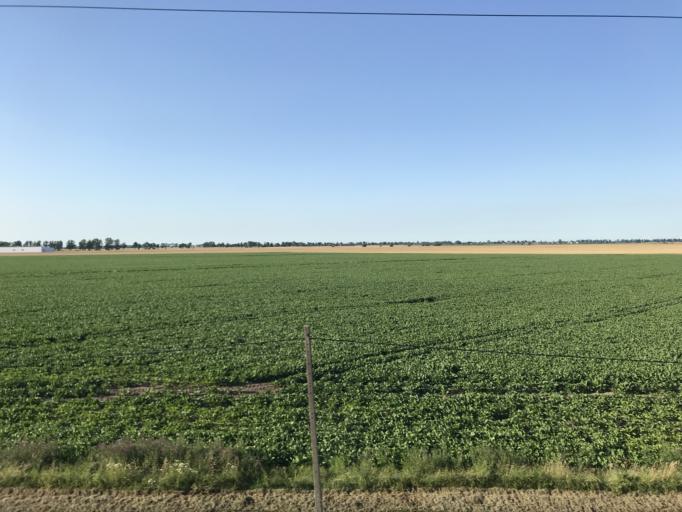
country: PL
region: Pomeranian Voivodeship
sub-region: Powiat malborski
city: Lisewo Malborskie
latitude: 54.0908
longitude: 18.8413
